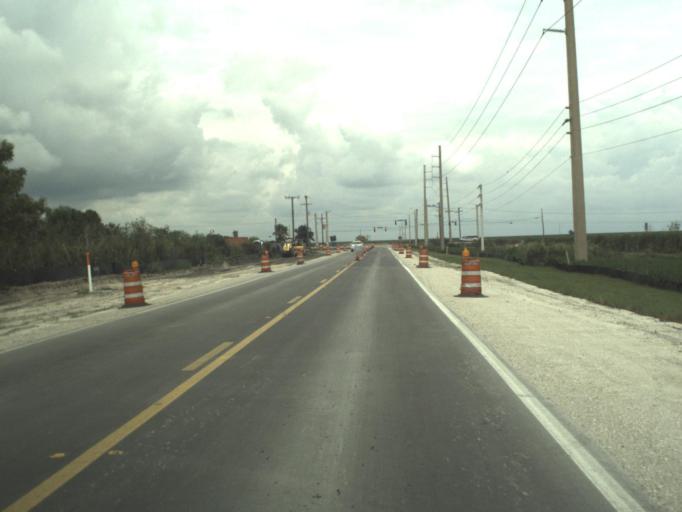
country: US
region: Florida
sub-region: Palm Beach County
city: Belle Glade
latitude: 26.7257
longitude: -80.6811
